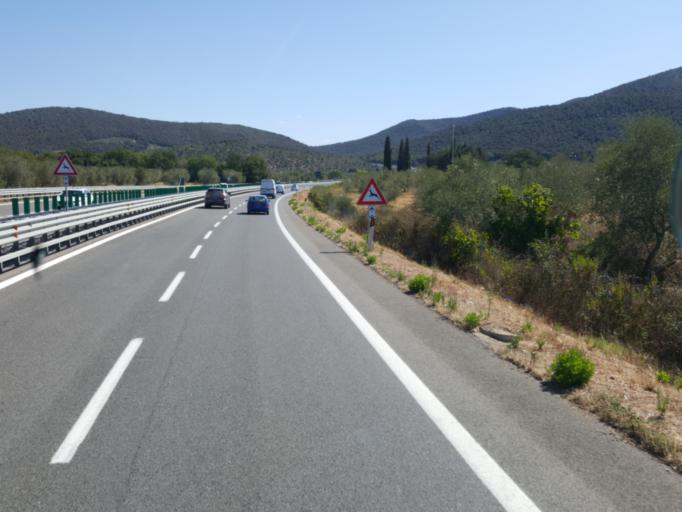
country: IT
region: Tuscany
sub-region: Provincia di Grosseto
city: Bagno Roselle
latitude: 42.8522
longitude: 11.1625
